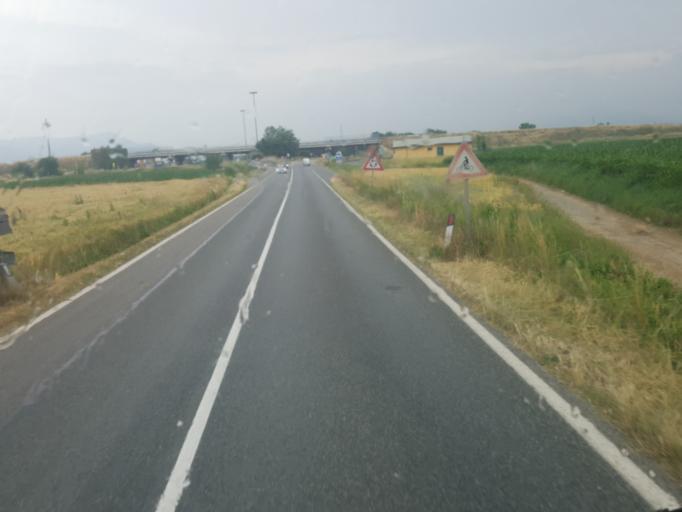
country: IT
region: Piedmont
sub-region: Provincia di Torino
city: Orbassano
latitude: 44.9786
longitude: 7.5559
